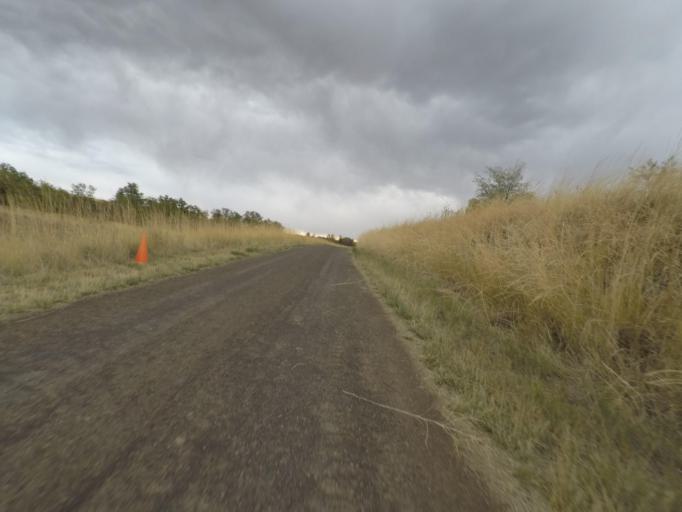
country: US
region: Washington
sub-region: Walla Walla County
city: Walla Walla East
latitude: 46.0787
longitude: -118.2546
